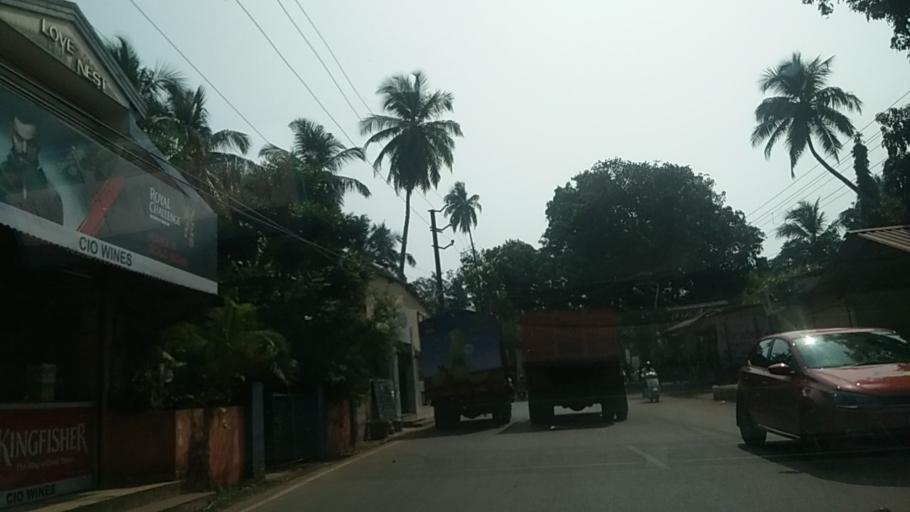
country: IN
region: Goa
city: Calangute
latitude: 15.5643
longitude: 73.7648
